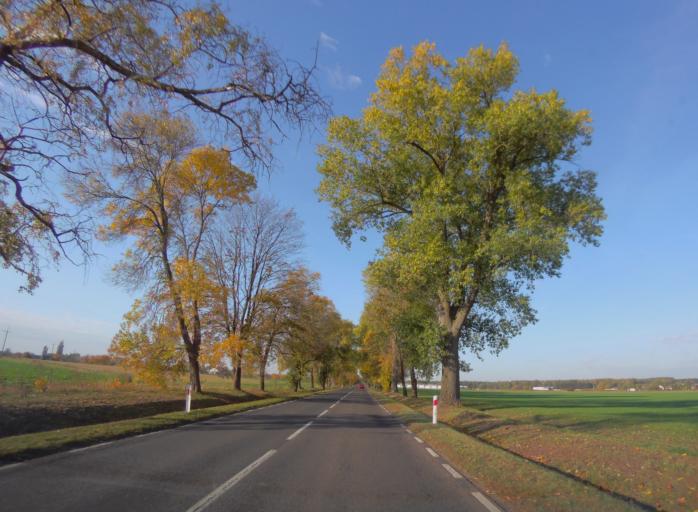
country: PL
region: Masovian Voivodeship
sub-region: Powiat siedlecki
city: Mordy
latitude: 52.2020
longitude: 22.5025
